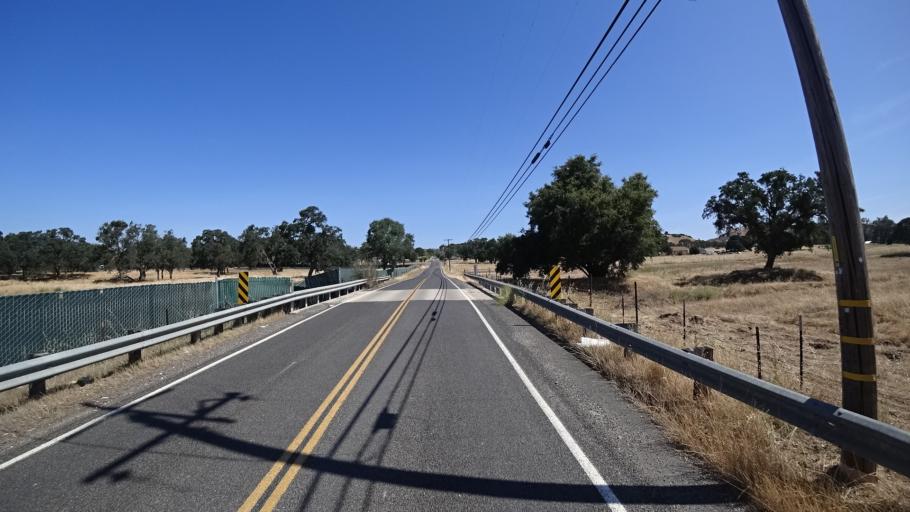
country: US
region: California
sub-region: Calaveras County
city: Rancho Calaveras
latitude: 38.1800
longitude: -120.8906
